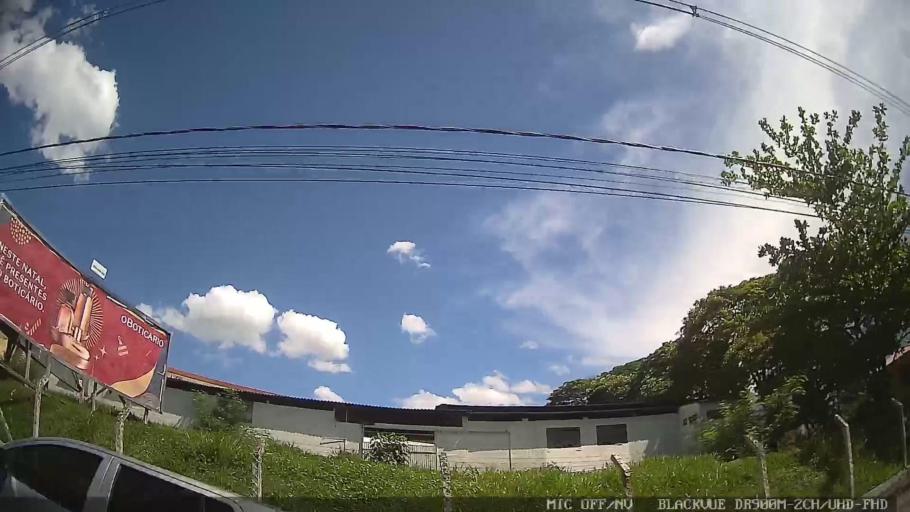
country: BR
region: Sao Paulo
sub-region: Pedreira
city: Pedreira
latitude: -22.7417
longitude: -46.8970
